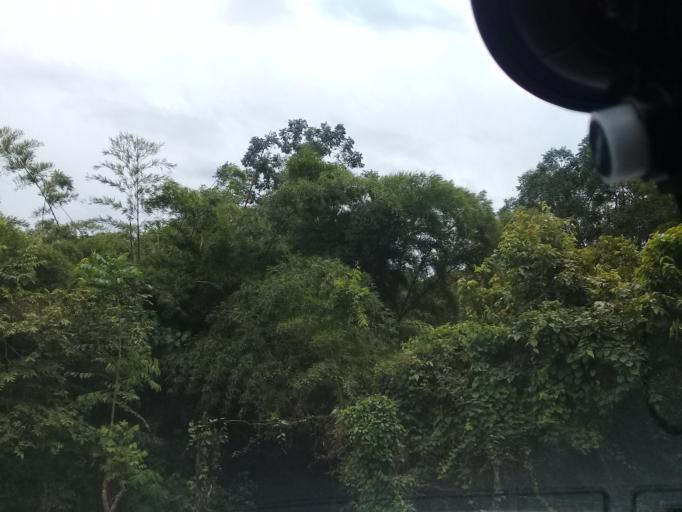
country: MX
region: Veracruz
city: Platon Sanchez
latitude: 21.2152
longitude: -98.3705
